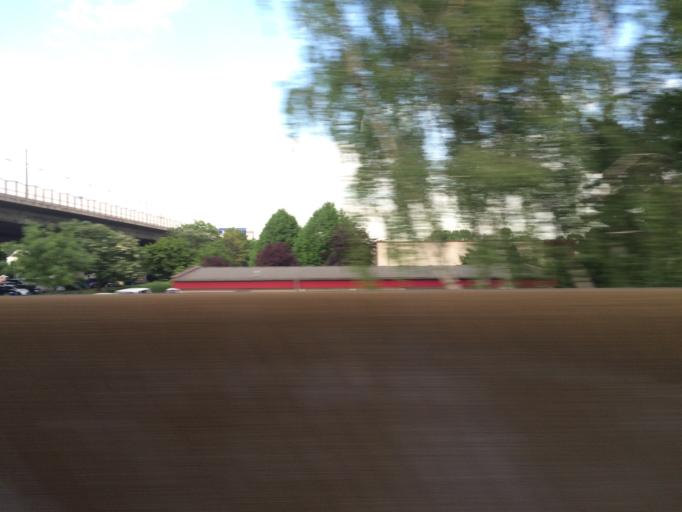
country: DE
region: North Rhine-Westphalia
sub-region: Regierungsbezirk Koln
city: Leverkusen
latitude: 51.0366
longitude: 6.9904
